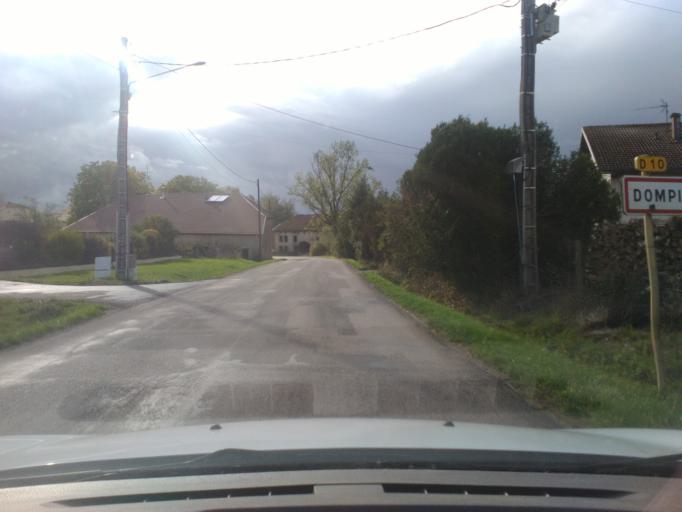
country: FR
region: Lorraine
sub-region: Departement des Vosges
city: Aydoilles
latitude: 48.2531
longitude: 6.5689
